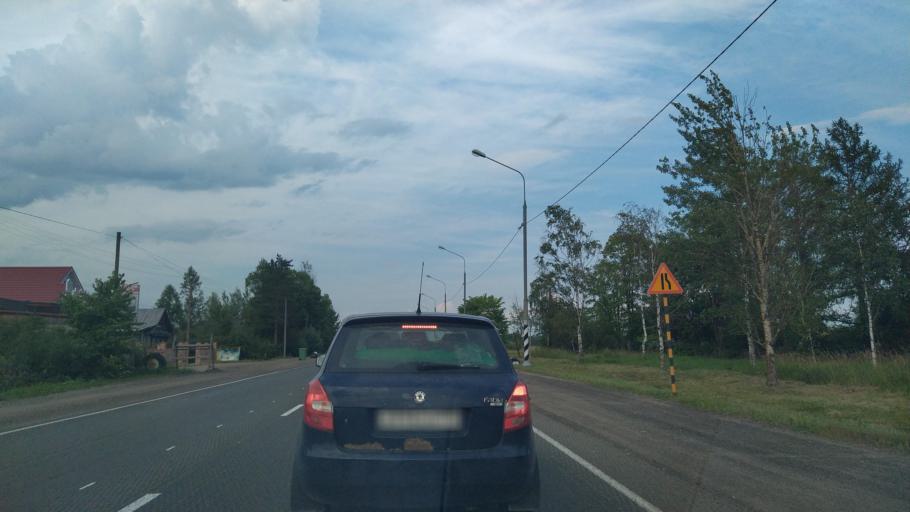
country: RU
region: Novgorod
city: Pankovka
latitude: 58.3871
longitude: 31.0243
